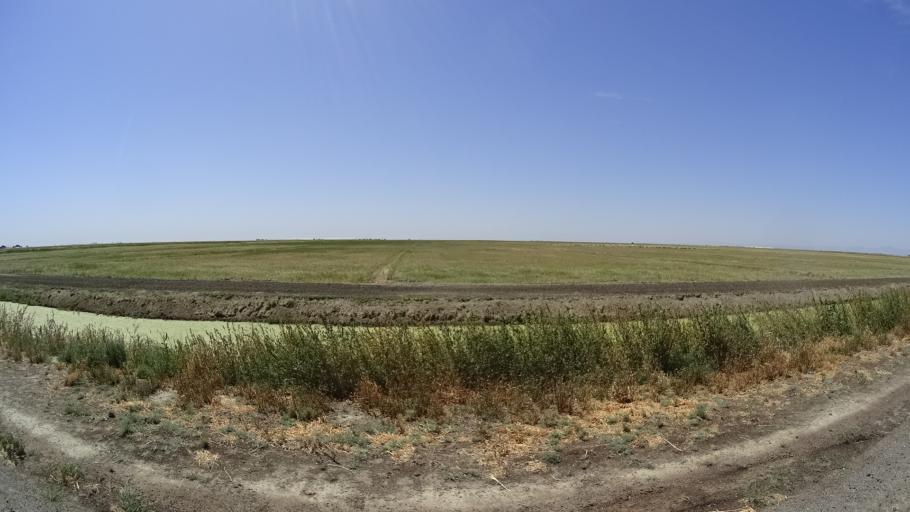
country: US
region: California
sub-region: Kings County
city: Stratford
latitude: 36.1893
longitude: -119.7019
